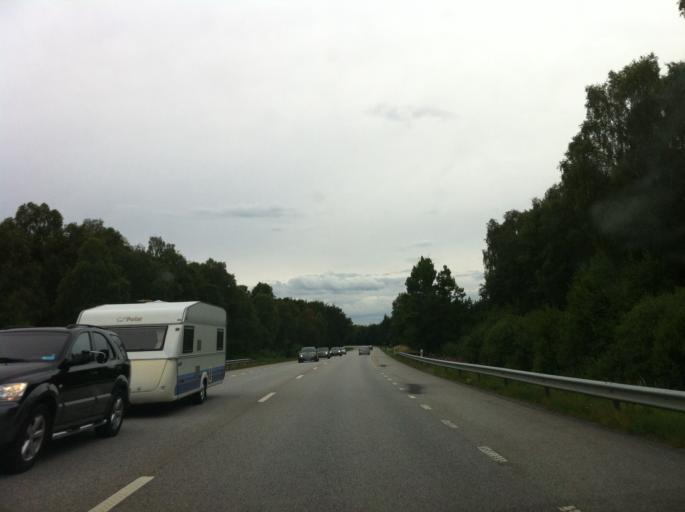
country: SE
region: Skane
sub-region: Hassleholms Kommun
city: Sosdala
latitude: 55.9862
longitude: 13.6130
